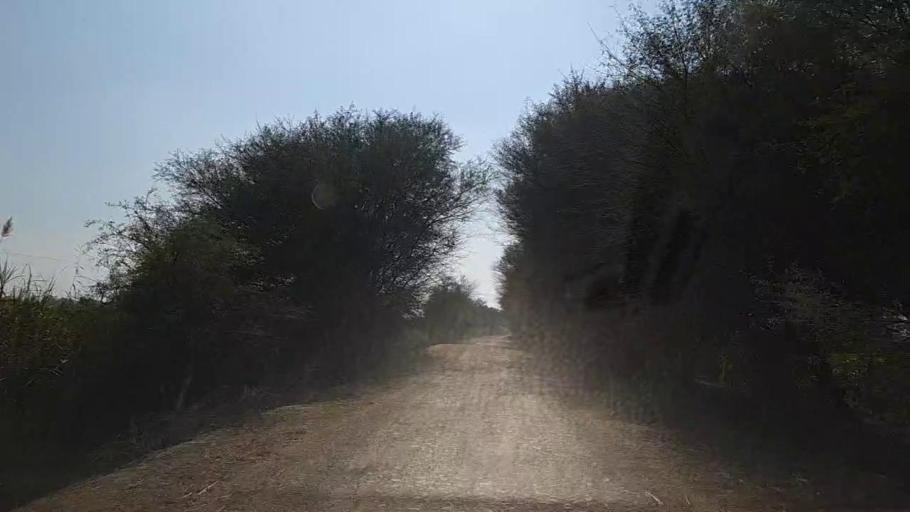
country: PK
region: Sindh
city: Daur
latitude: 26.5056
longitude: 68.3402
